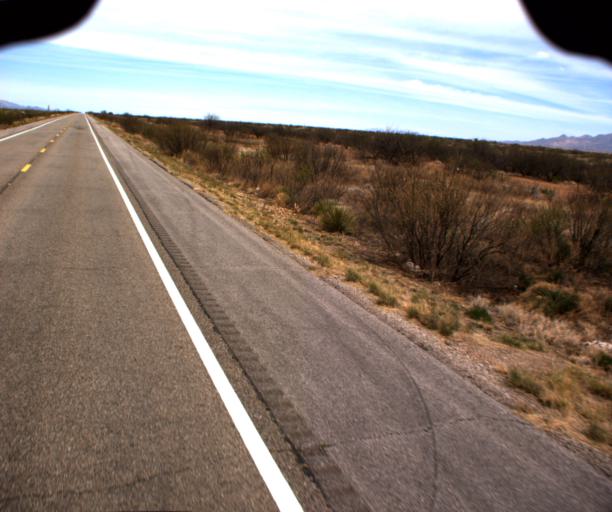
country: US
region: Arizona
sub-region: Cochise County
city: Pirtleville
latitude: 31.5037
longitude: -109.6369
